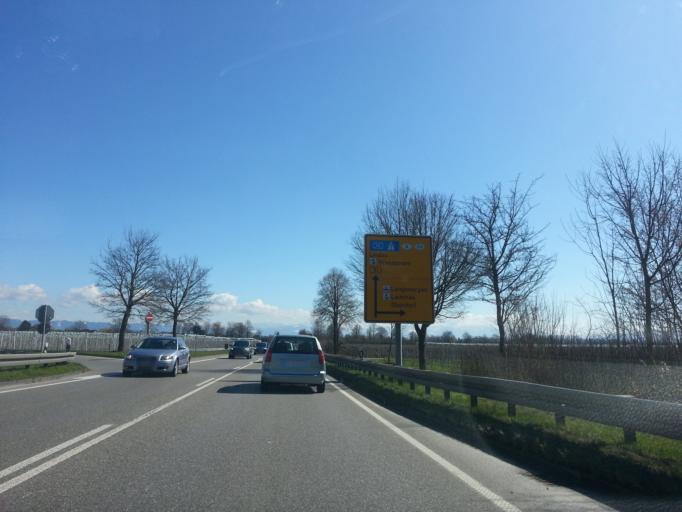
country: DE
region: Baden-Wuerttemberg
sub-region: Tuebingen Region
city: Eriskirch
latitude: 47.6171
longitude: 9.5658
